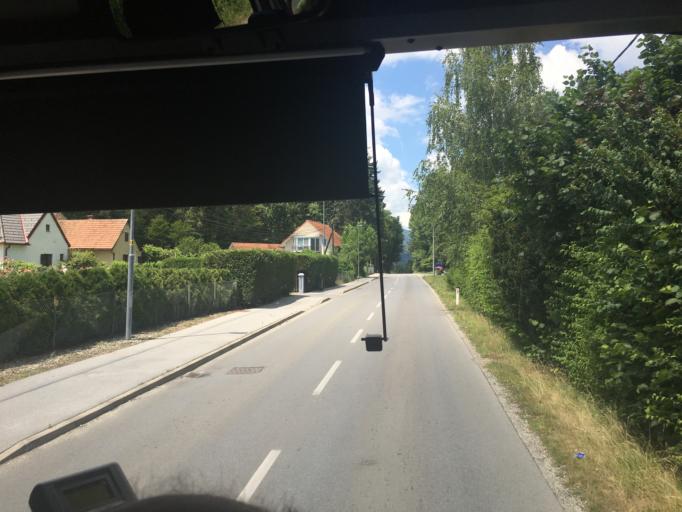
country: SI
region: Maribor
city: Pekre
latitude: 46.5435
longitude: 15.6028
